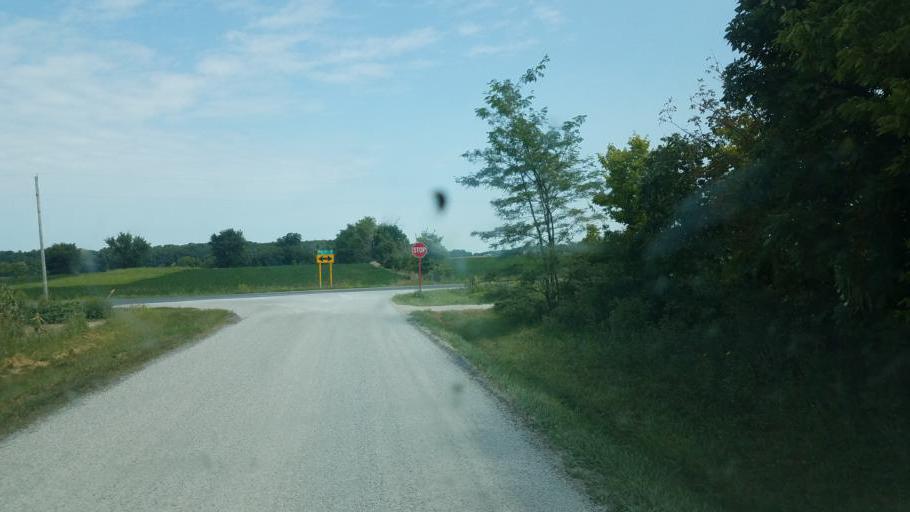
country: US
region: Ohio
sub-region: Delaware County
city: Ashley
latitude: 40.4576
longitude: -83.0580
